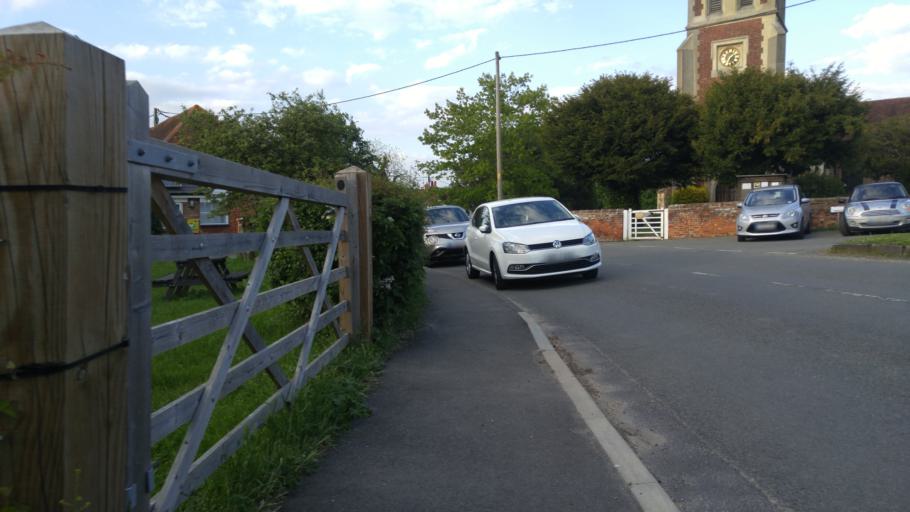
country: GB
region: England
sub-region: Essex
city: Tiptree
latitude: 51.8366
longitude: 0.7508
